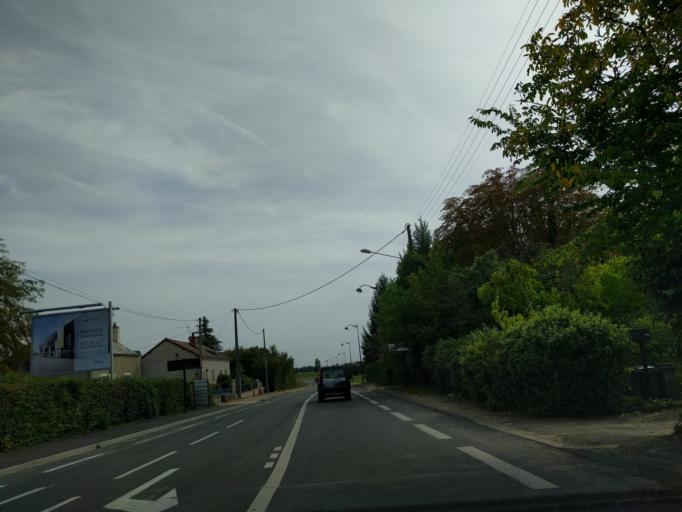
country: FR
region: Centre
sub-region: Departement du Cher
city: Bourges
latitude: 47.0602
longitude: 2.4244
